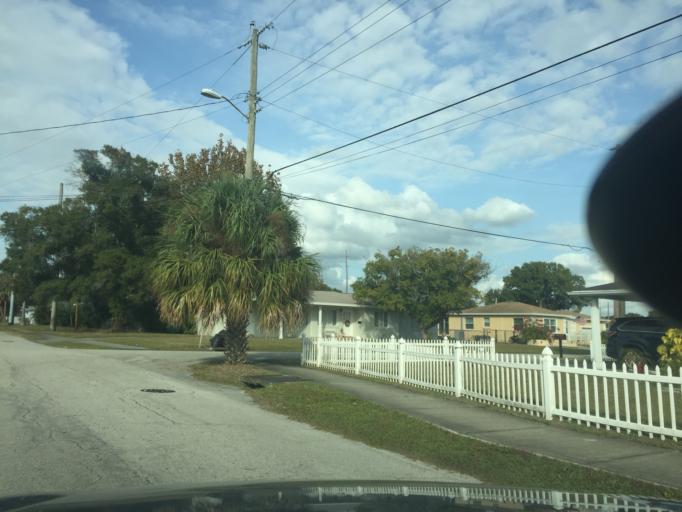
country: US
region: Florida
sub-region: Hillsborough County
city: Tampa
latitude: 27.9497
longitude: -82.4892
